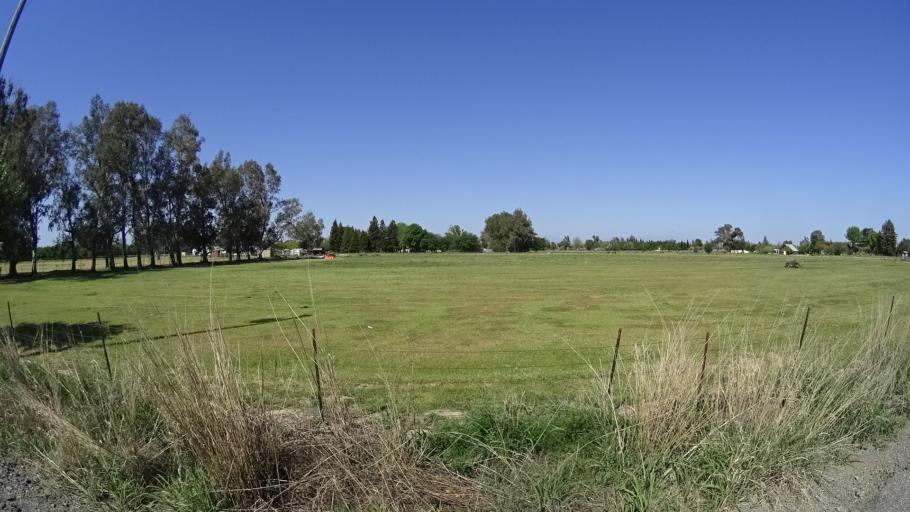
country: US
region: California
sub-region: Glenn County
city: Orland
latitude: 39.7197
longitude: -122.1853
